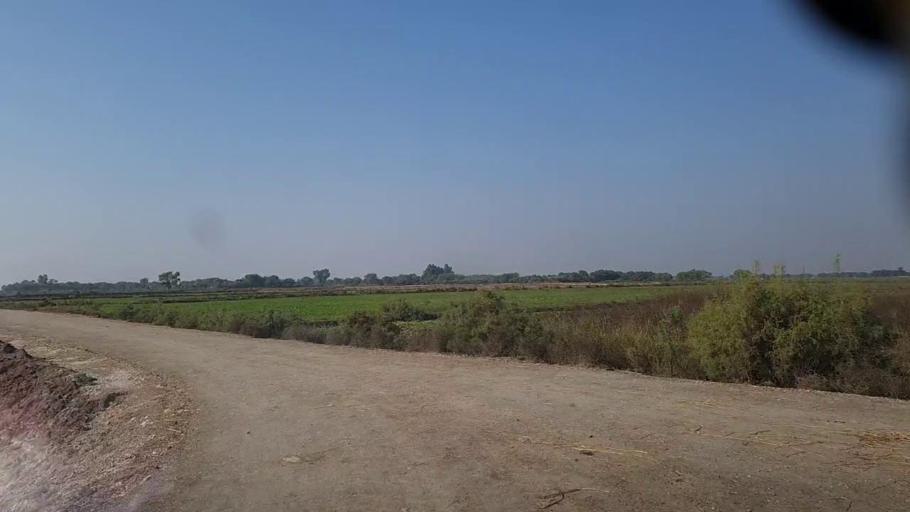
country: PK
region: Sindh
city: Jacobabad
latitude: 28.3113
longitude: 68.5619
